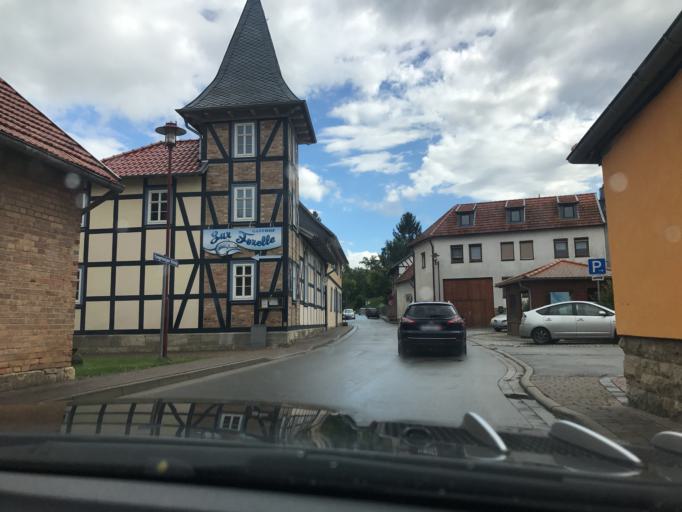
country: DE
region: Thuringia
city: Flarchheim
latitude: 51.1258
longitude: 10.4793
